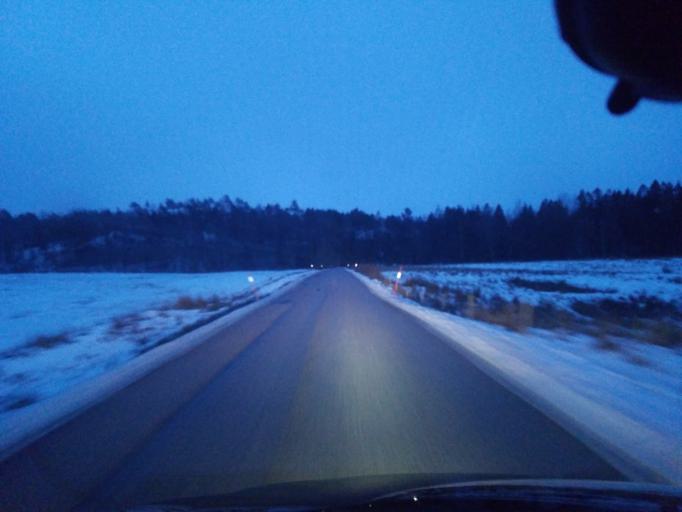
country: SE
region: Vaestra Goetaland
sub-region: Orust
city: Henan
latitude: 58.2890
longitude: 11.5817
